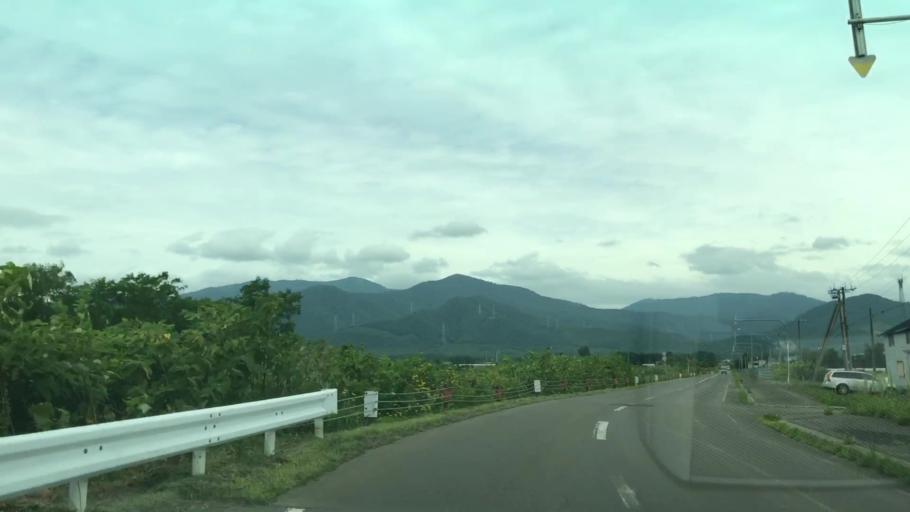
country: JP
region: Hokkaido
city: Iwanai
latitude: 43.0176
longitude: 140.5688
